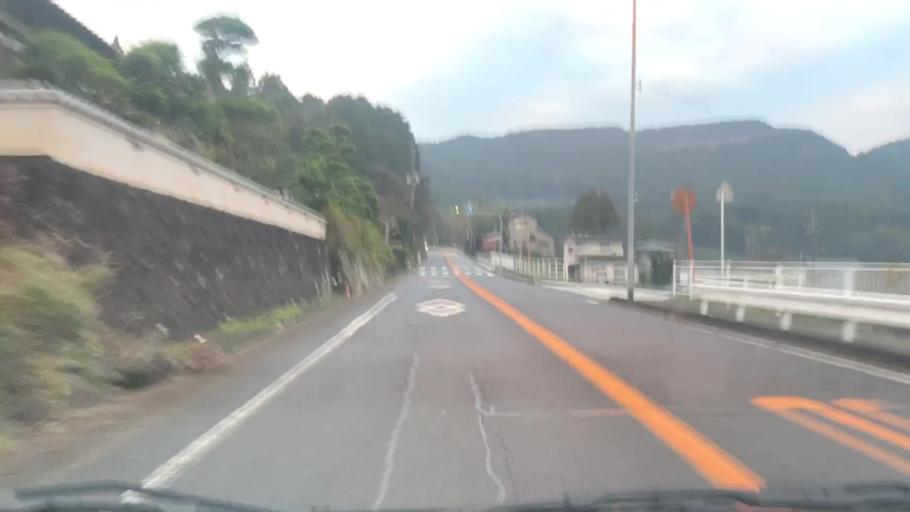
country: JP
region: Saga Prefecture
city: Ureshinomachi-shimojuku
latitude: 33.0748
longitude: 129.9625
